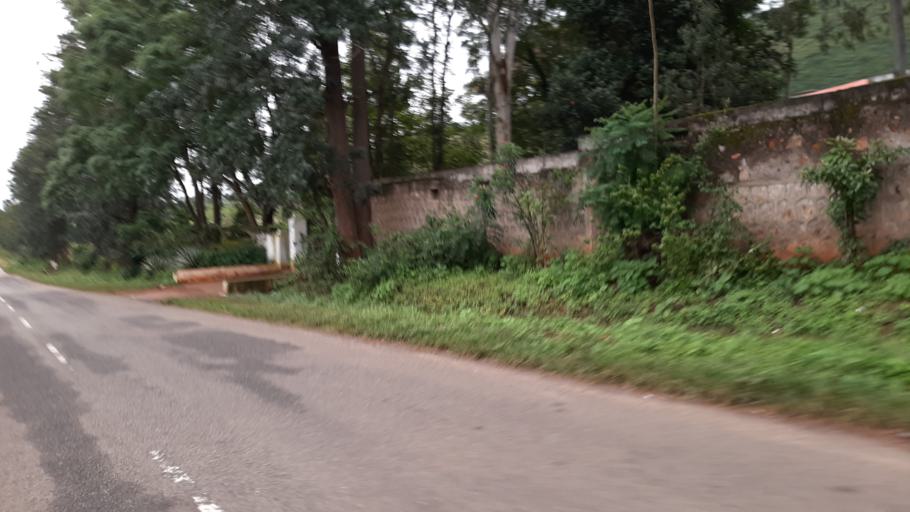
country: IN
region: Andhra Pradesh
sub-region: Vizianagaram District
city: Salur
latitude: 18.2930
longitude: 82.9188
